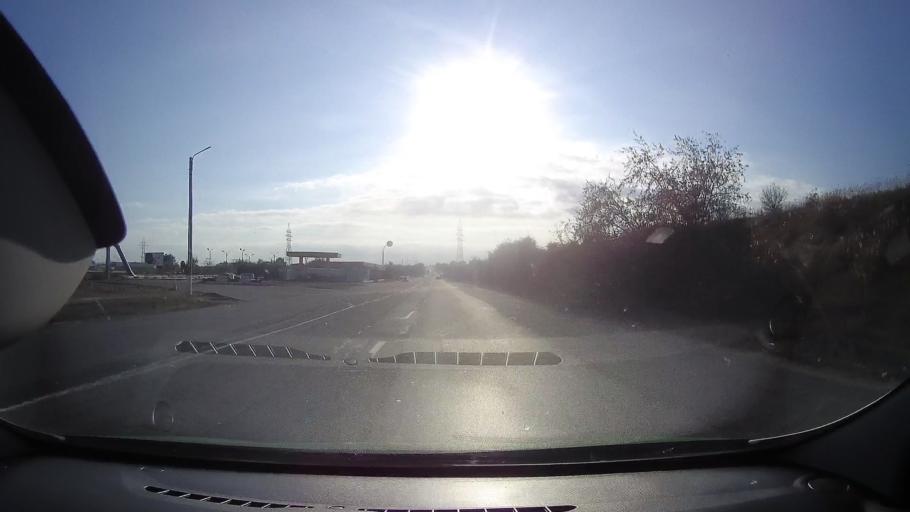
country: RO
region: Constanta
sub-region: Comuna Navodari
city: Navodari
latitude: 44.3295
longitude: 28.6284
